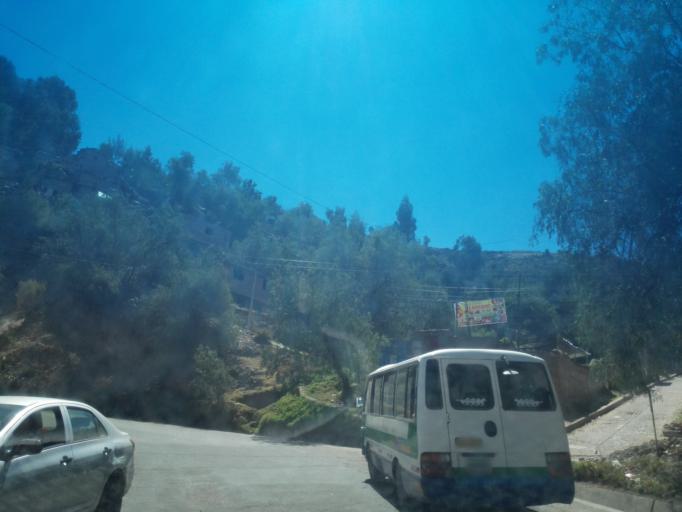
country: PE
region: Ayacucho
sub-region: Provincia de Huamanga
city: Ayacucho
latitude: -13.1581
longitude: -74.2368
